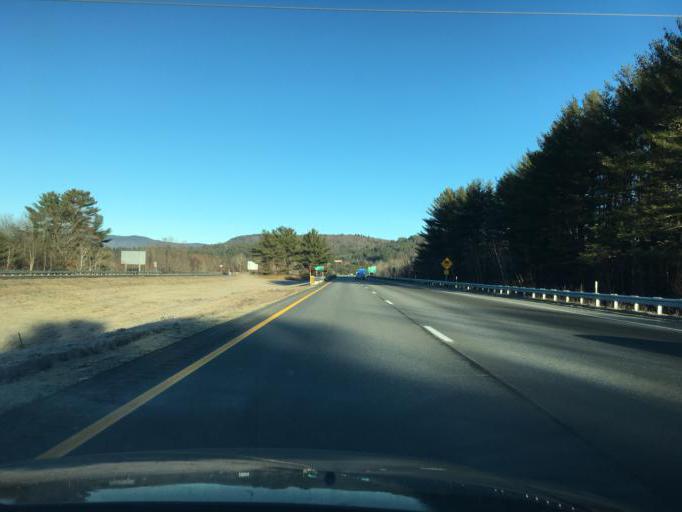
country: US
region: New Hampshire
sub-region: Grafton County
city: Plymouth
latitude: 43.7645
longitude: -71.6797
